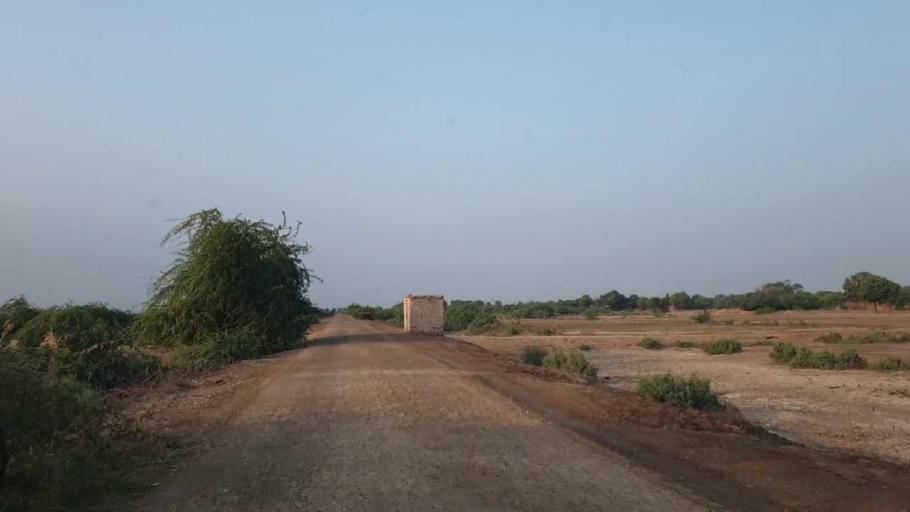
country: PK
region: Sindh
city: Tando Ghulam Ali
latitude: 25.0607
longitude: 68.9605
